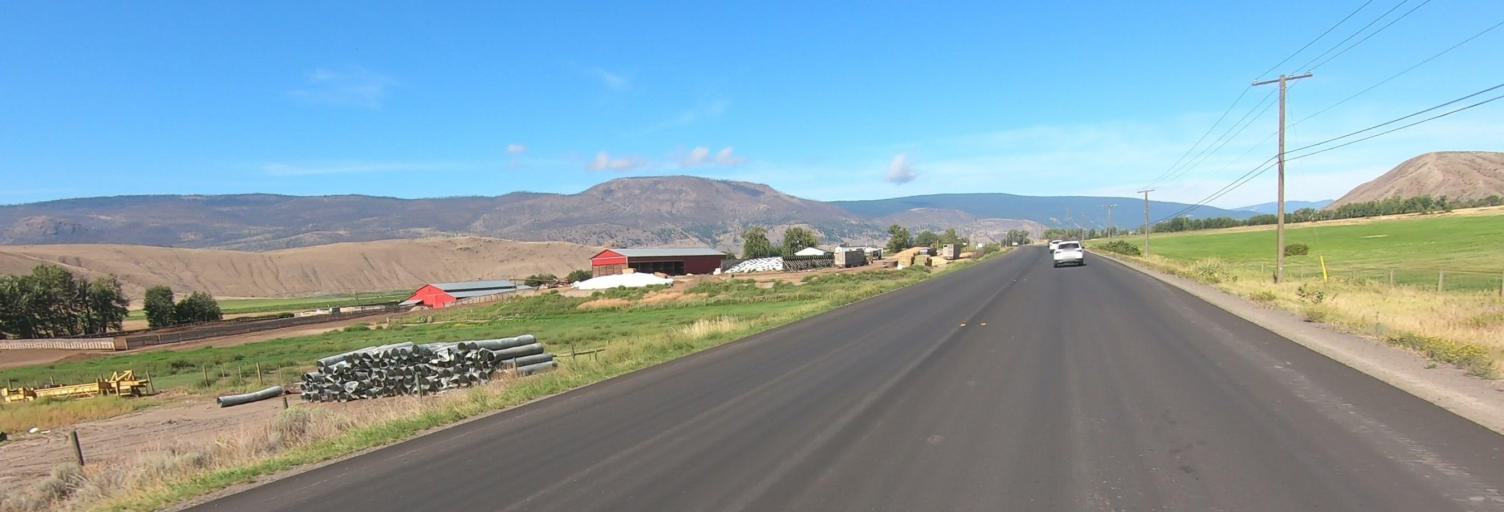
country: CA
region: British Columbia
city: Cache Creek
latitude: 50.8034
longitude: -121.2746
